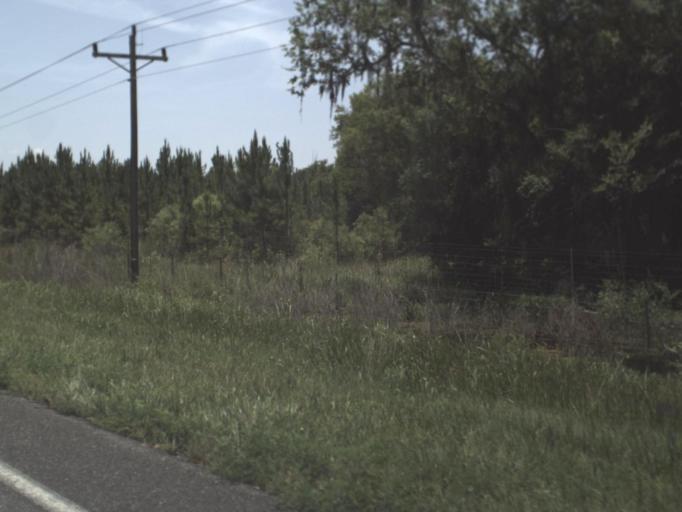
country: US
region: Florida
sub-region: Taylor County
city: Steinhatchee
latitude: 29.8498
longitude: -83.3792
